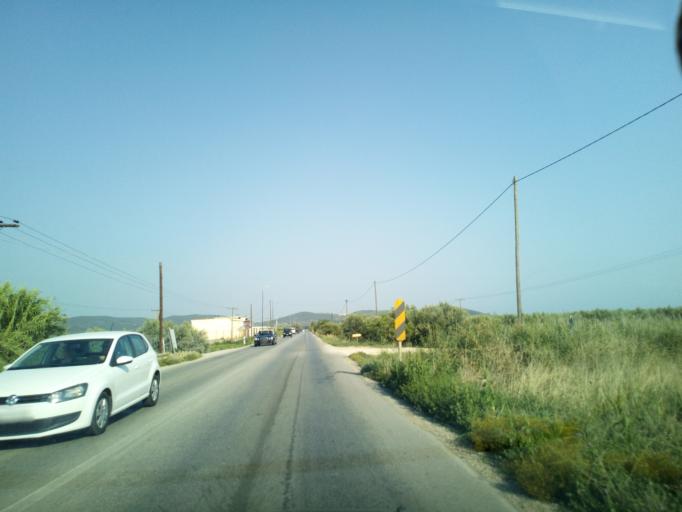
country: GR
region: Central Macedonia
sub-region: Nomos Chalkidikis
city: Ormylia
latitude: 40.2609
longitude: 23.5233
